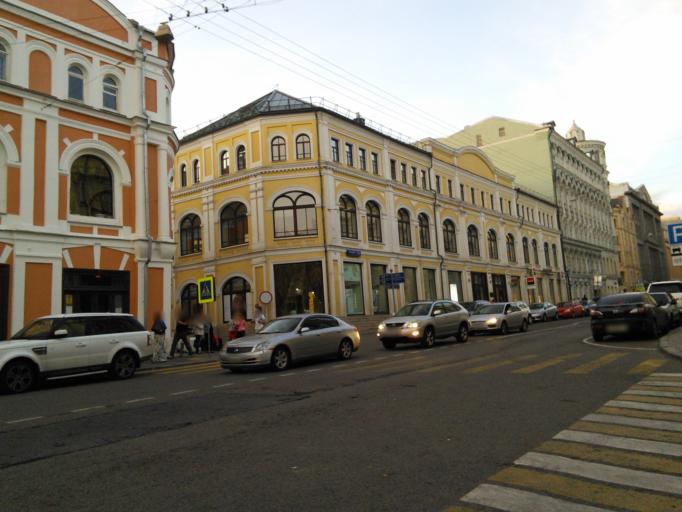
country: RU
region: Moscow
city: Moscow
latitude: 55.7542
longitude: 37.6242
